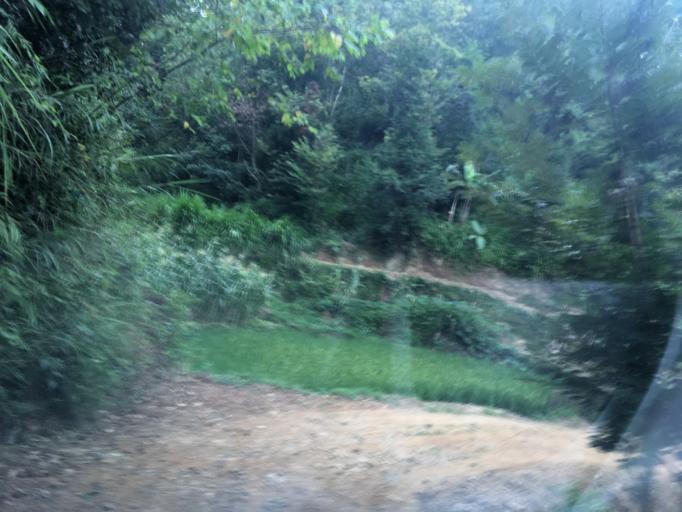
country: CN
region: Guangxi Zhuangzu Zizhiqu
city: Xinzhou
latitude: 25.1654
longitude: 105.6854
